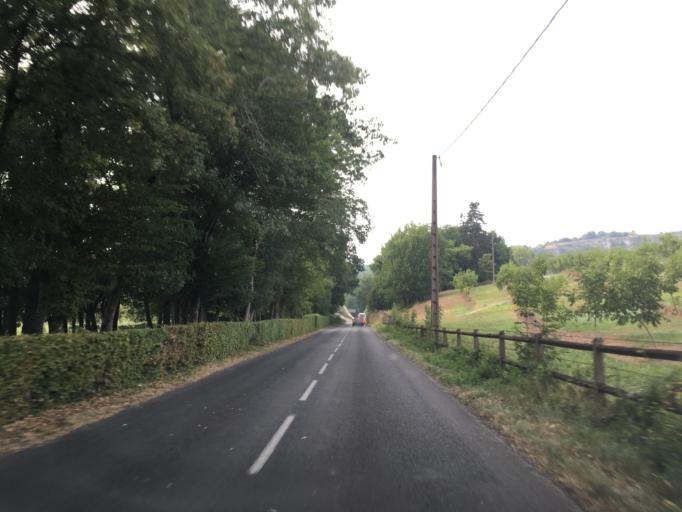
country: FR
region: Midi-Pyrenees
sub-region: Departement du Lot
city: Souillac
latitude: 44.8502
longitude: 1.5295
